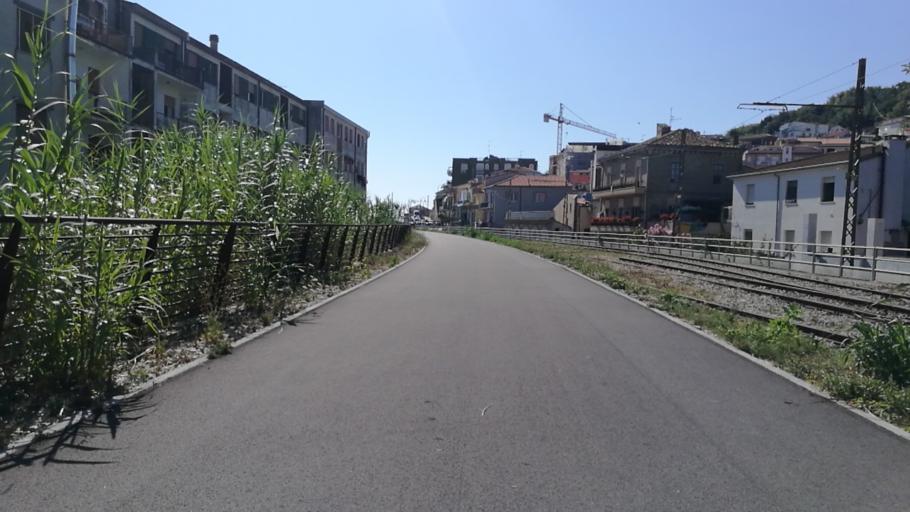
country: IT
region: Abruzzo
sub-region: Provincia di Chieti
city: Marina di San Vito
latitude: 42.3094
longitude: 14.4443
